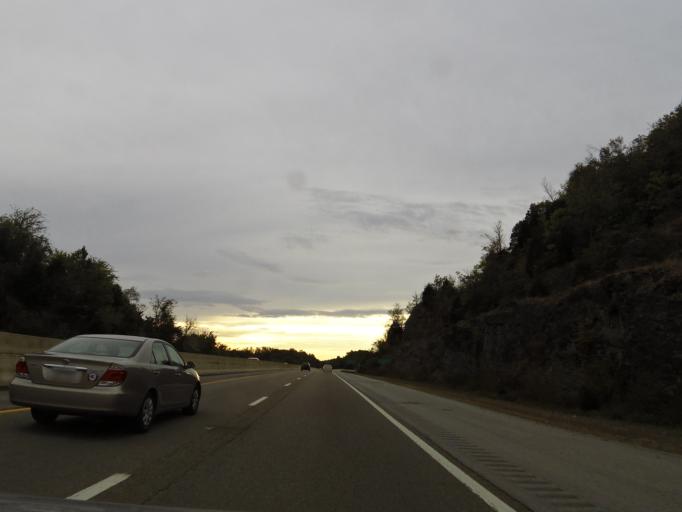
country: US
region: Tennessee
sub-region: Blount County
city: Louisville
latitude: 35.8497
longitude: -84.0046
